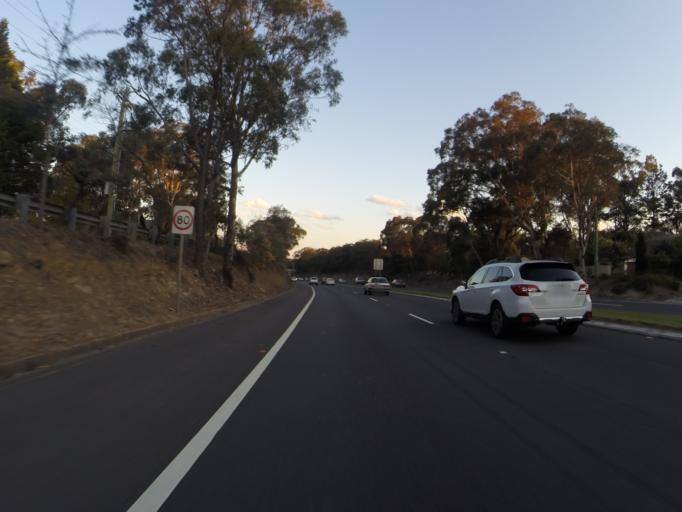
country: AU
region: New South Wales
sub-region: Blue Mountains Municipality
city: Glenbrook
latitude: -33.7588
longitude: 150.6125
